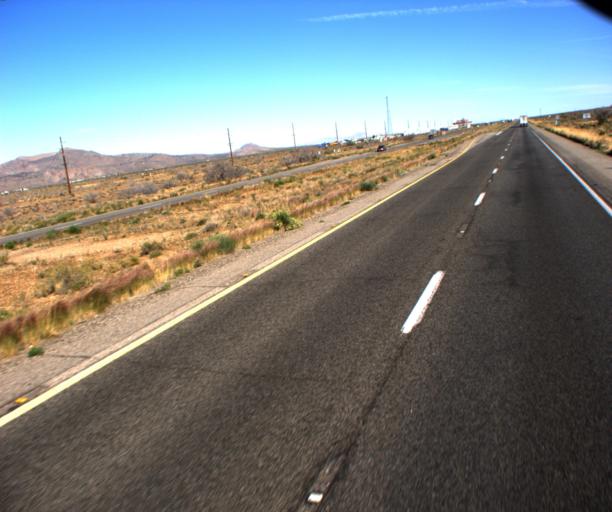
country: US
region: Arizona
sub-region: Mohave County
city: Golden Valley
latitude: 35.3301
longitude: -114.2108
